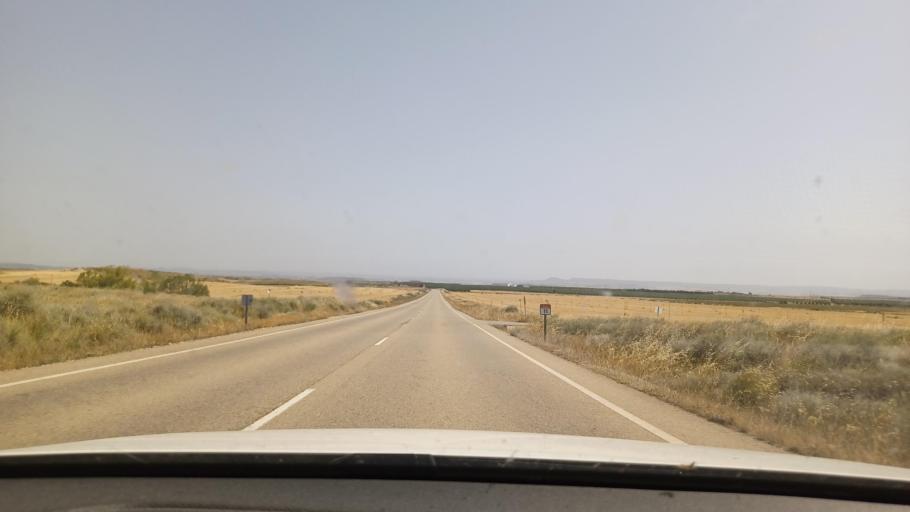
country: ES
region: Aragon
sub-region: Provincia de Zaragoza
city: Chiprana
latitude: 41.3171
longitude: -0.0766
